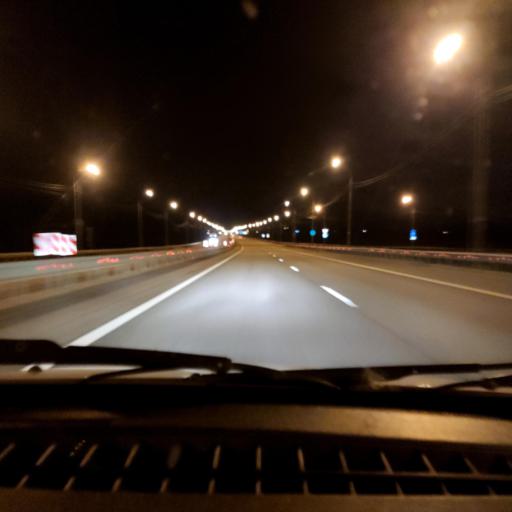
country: RU
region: Lipetsk
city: Zadonsk
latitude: 52.3700
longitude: 38.9160
